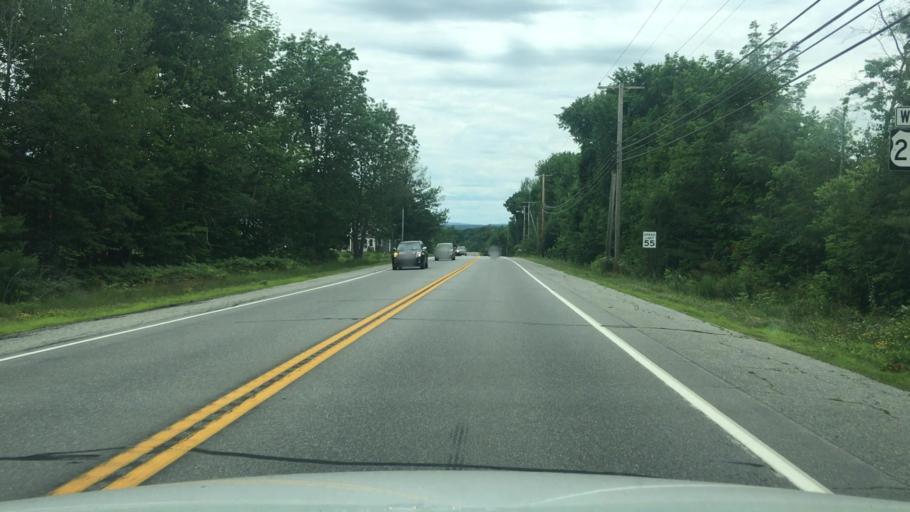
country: US
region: Maine
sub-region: Kennebec County
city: Sidney
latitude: 44.3356
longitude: -69.6875
